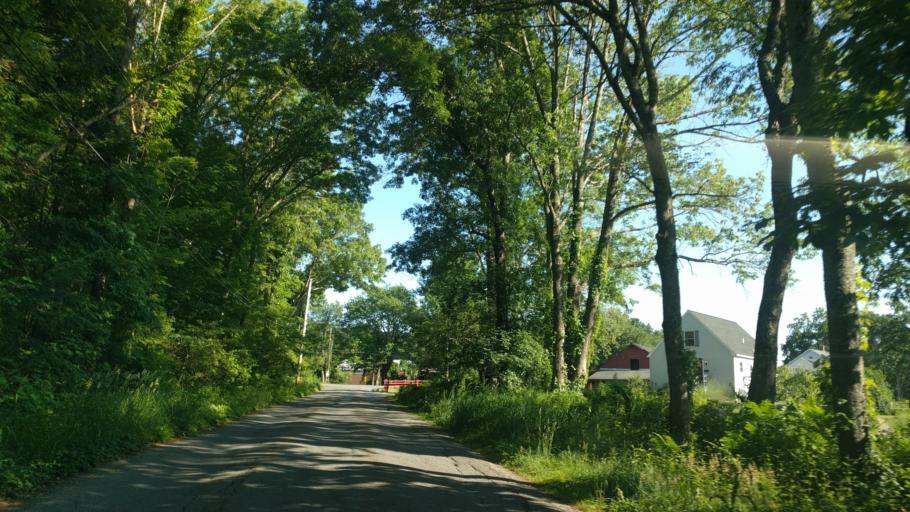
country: US
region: Massachusetts
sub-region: Worcester County
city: Oxford
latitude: 42.1436
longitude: -71.8449
